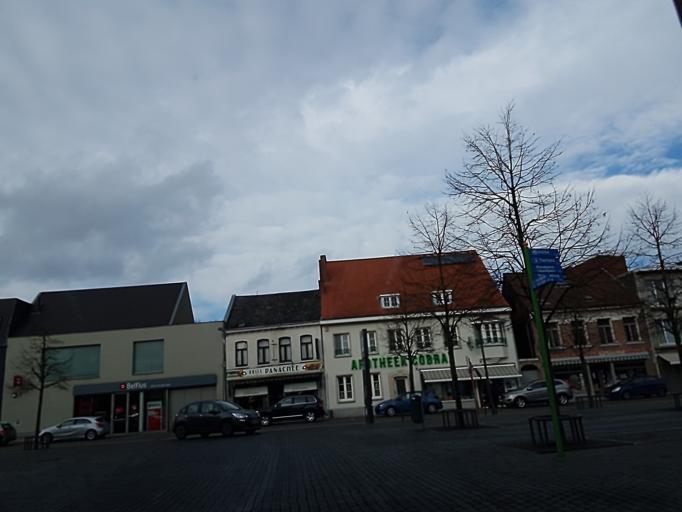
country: BE
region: Flanders
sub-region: Provincie Antwerpen
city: Mol
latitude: 51.1832
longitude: 5.1141
